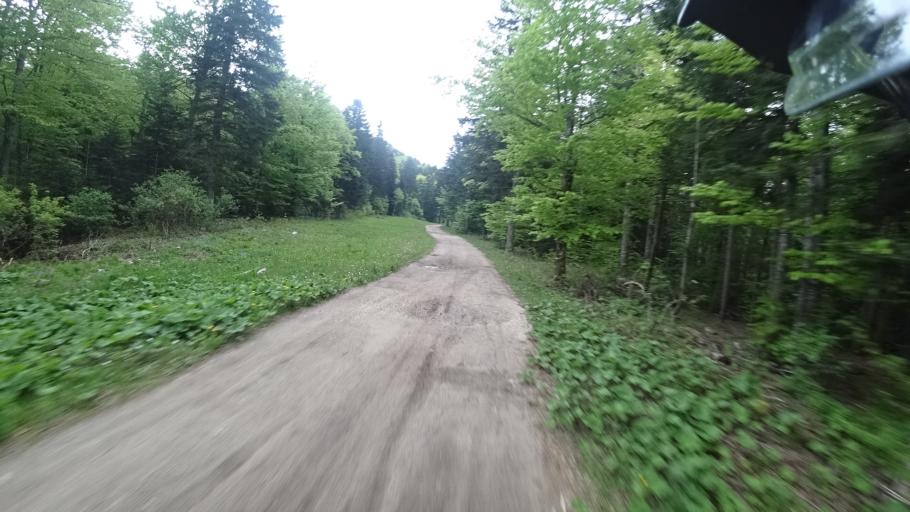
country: HR
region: Karlovacka
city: Plaski
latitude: 44.9209
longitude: 15.4277
